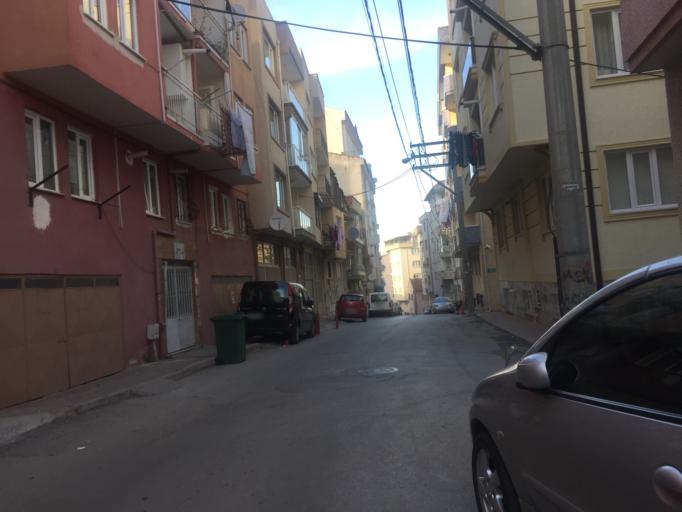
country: TR
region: Bursa
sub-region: Osmangazi
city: Bursa
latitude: 40.1869
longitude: 29.0838
